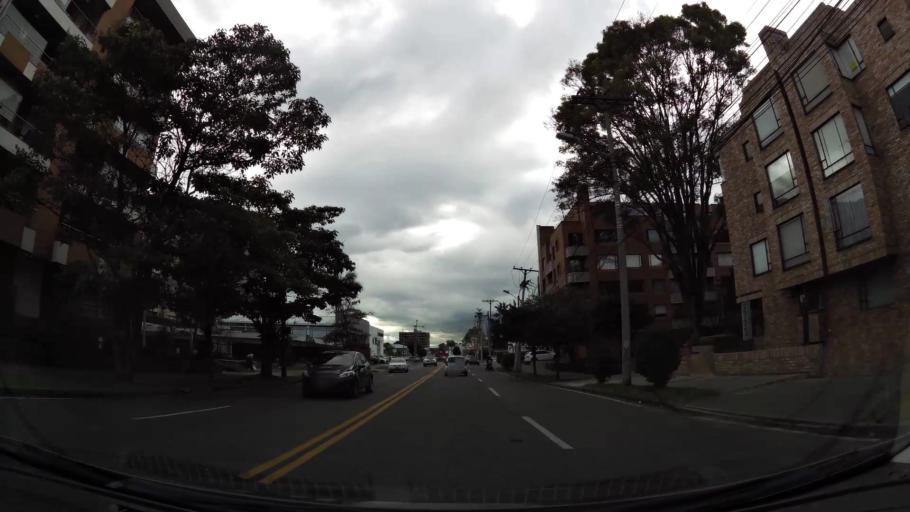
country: CO
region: Bogota D.C.
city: Barrio San Luis
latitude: 4.6911
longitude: -74.0551
